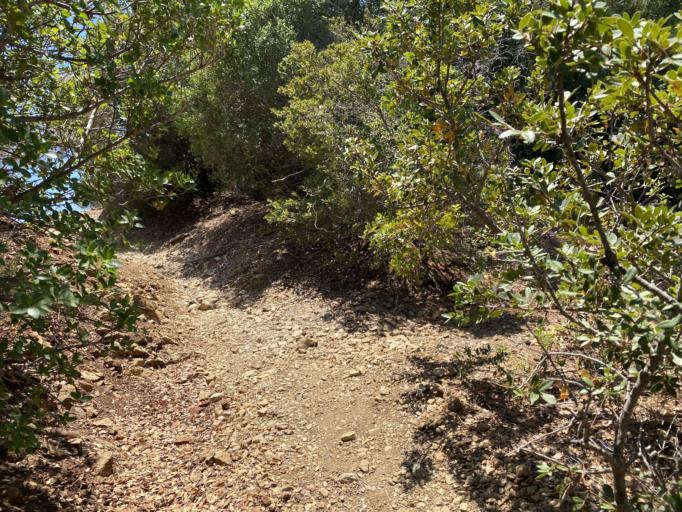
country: TR
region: Mugla
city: Goecek
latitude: 36.7077
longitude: 28.9348
